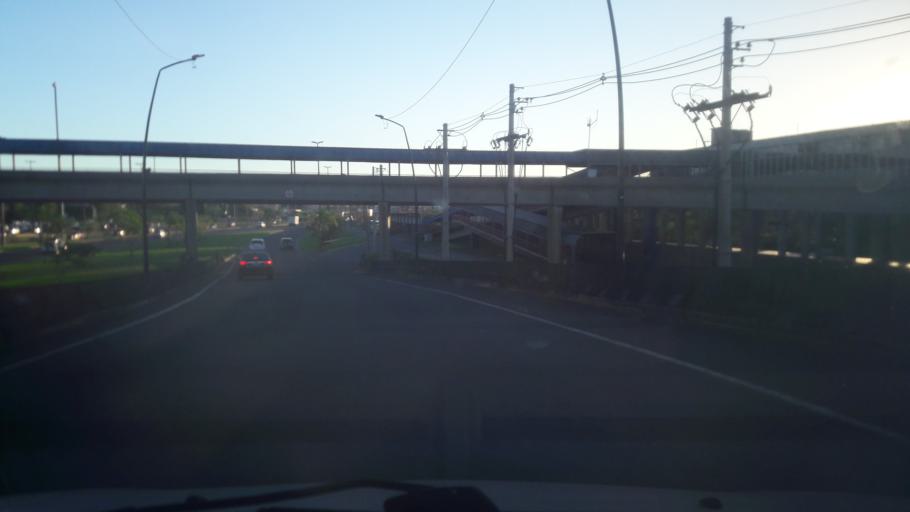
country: BR
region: Rio Grande do Sul
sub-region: Porto Alegre
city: Porto Alegre
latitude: -29.9875
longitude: -51.1825
